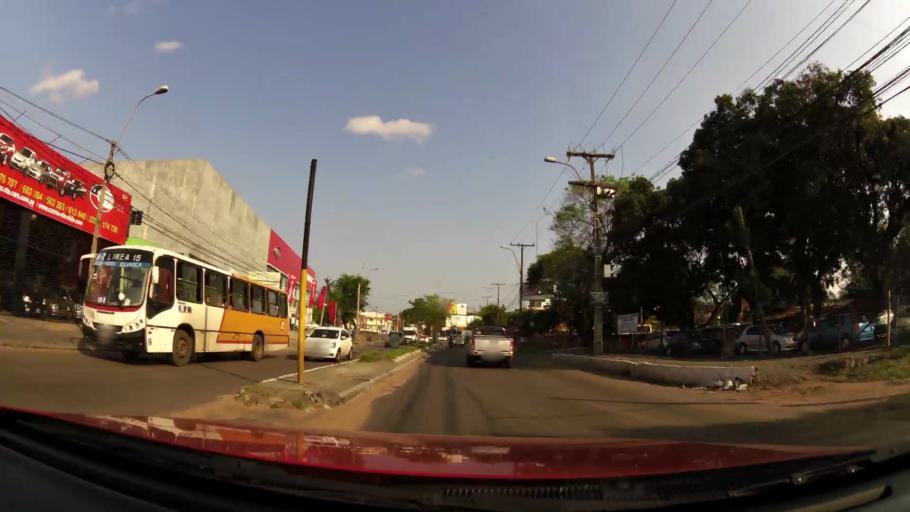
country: PY
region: Central
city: Lambare
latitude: -25.3332
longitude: -57.5908
